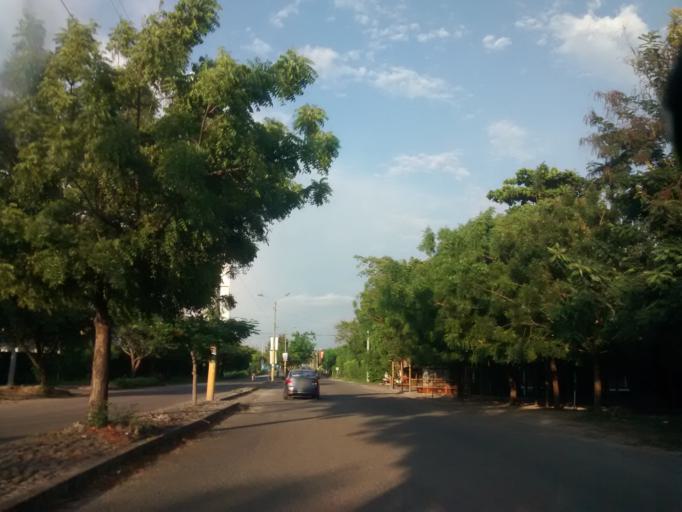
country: CO
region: Cundinamarca
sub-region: Girardot
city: Girardot City
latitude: 4.3030
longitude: -74.8157
